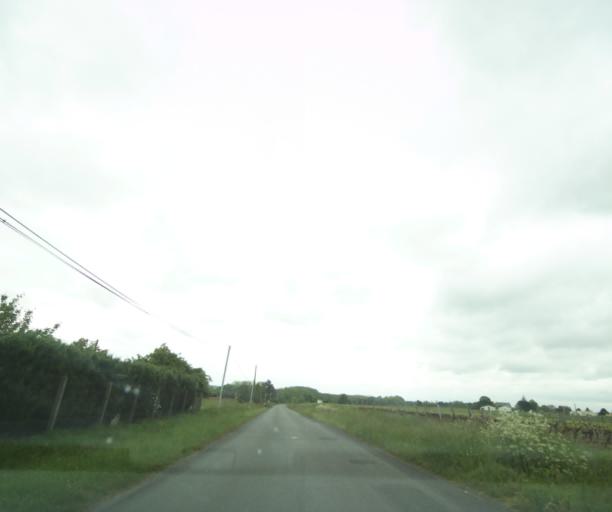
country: FR
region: Poitou-Charentes
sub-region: Departement de la Charente-Maritime
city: Chaniers
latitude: 45.7038
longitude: -0.5608
